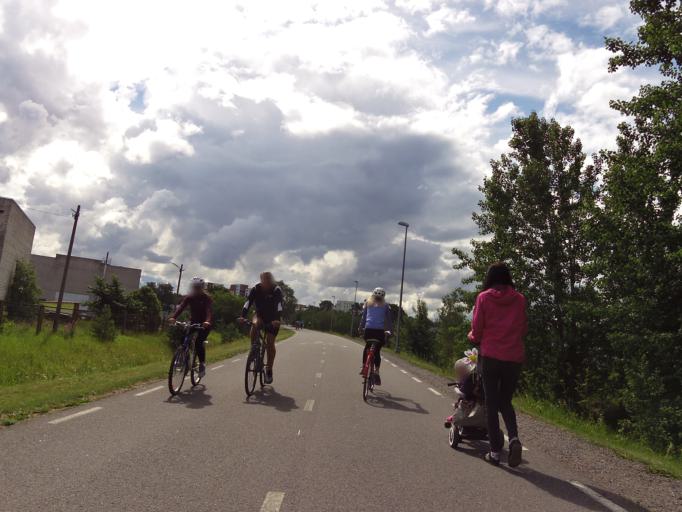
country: EE
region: Harju
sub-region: Saue vald
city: Laagri
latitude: 59.4022
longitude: 24.6436
